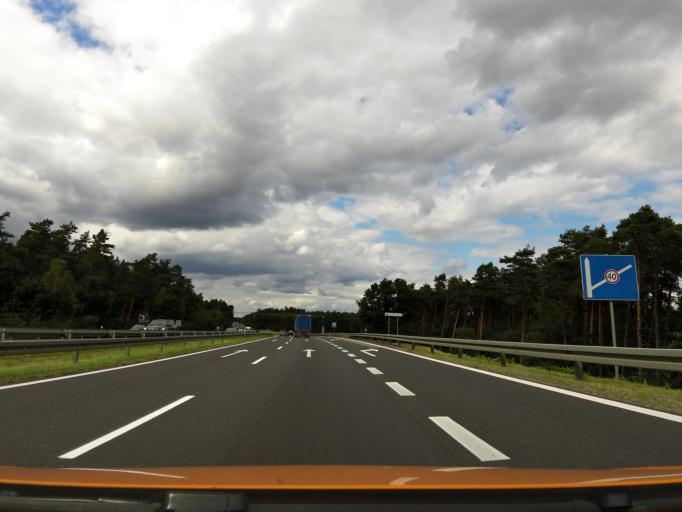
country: PL
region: West Pomeranian Voivodeship
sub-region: Powiat goleniowski
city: Goleniow
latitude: 53.5320
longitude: 14.8113
